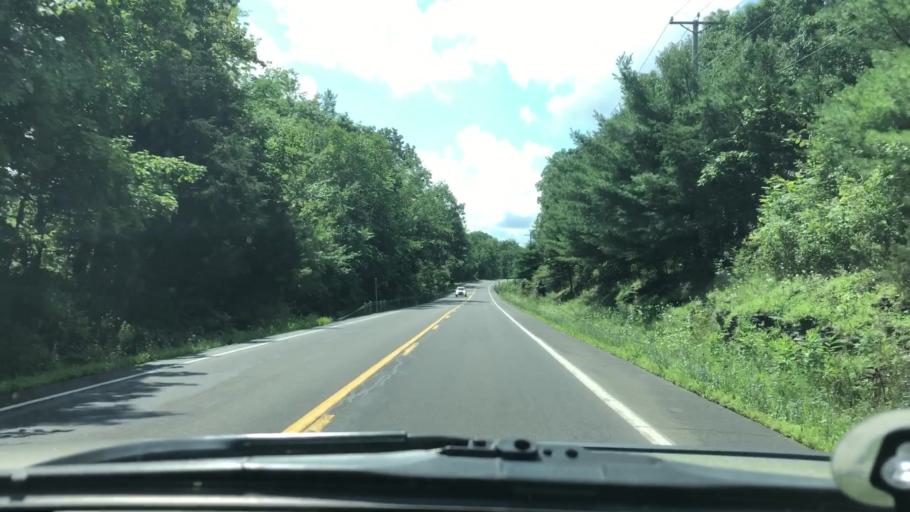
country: US
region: New York
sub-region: Greene County
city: Cairo
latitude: 42.2714
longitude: -73.9763
